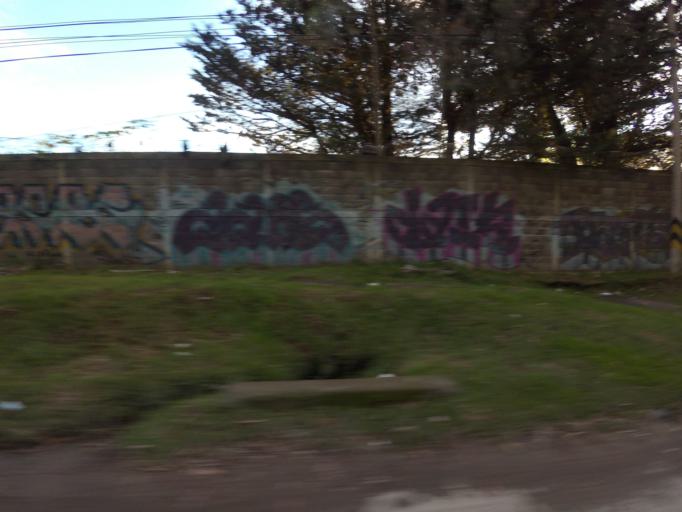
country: CO
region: Cundinamarca
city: La Calera
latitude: 4.7706
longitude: -74.0271
